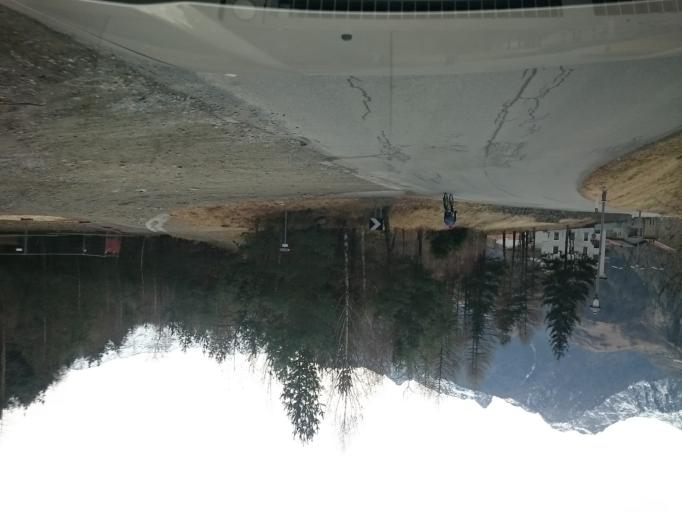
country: IT
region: Lombardy
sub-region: Provincia di Sondrio
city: Sondalo
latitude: 46.3564
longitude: 10.3542
